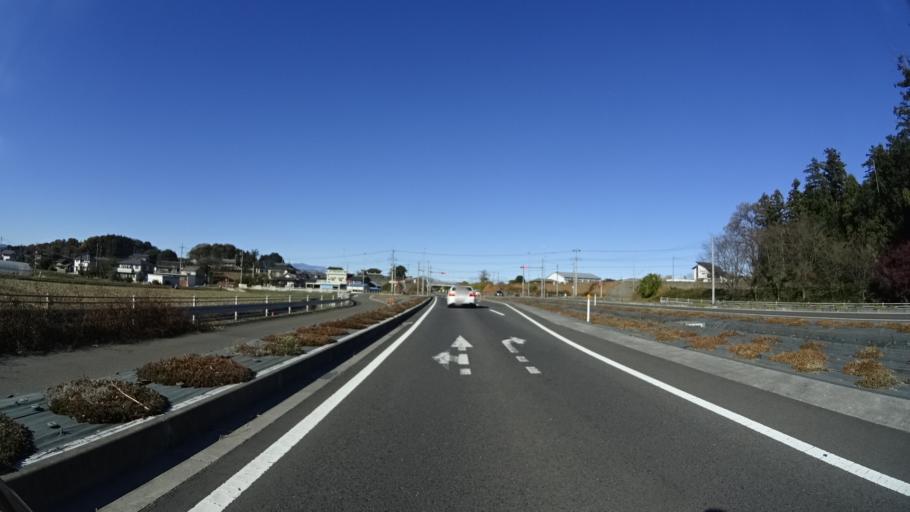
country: JP
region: Tochigi
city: Kanuma
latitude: 36.4902
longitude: 139.7530
